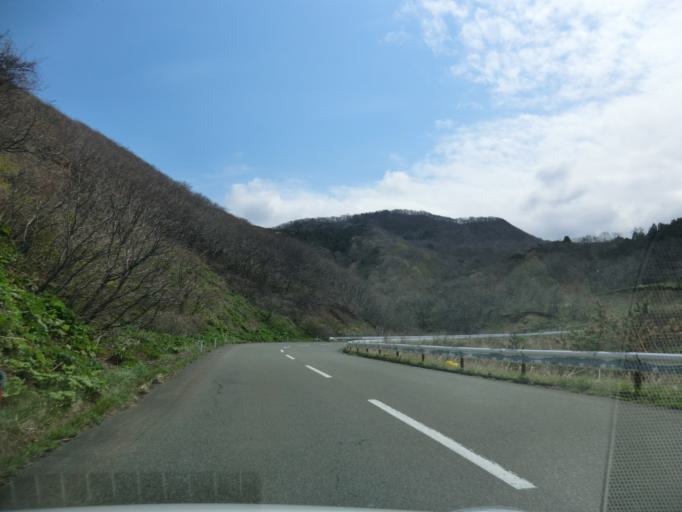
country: JP
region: Aomori
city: Mutsu
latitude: 41.3839
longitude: 140.8293
